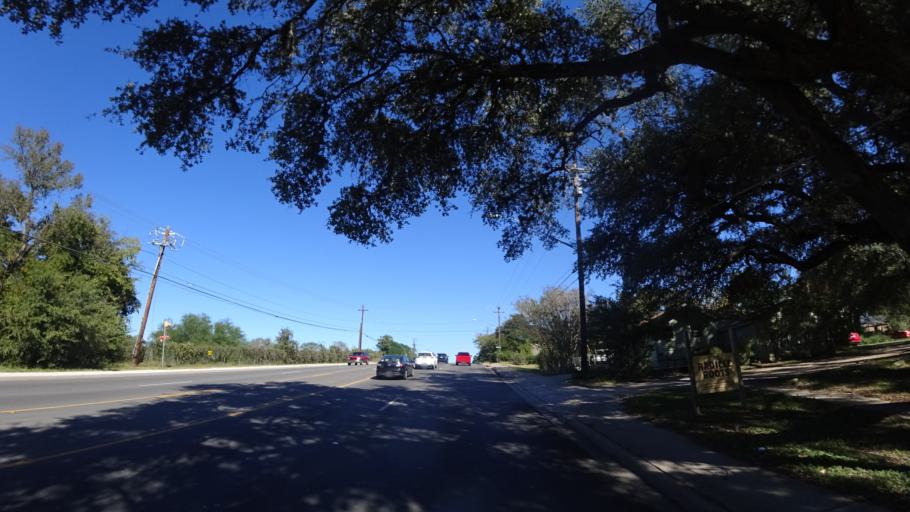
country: US
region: Texas
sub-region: Travis County
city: Austin
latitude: 30.2839
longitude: -97.6949
